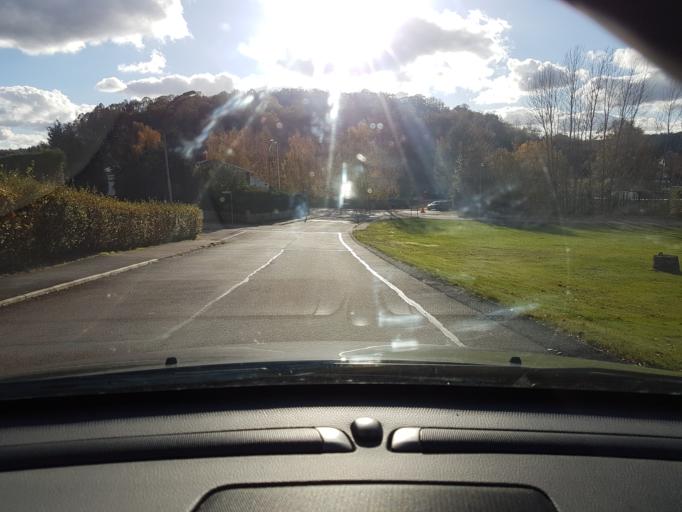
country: SE
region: Vaestra Goetaland
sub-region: Ale Kommun
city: Surte
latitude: 57.8300
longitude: 12.0209
